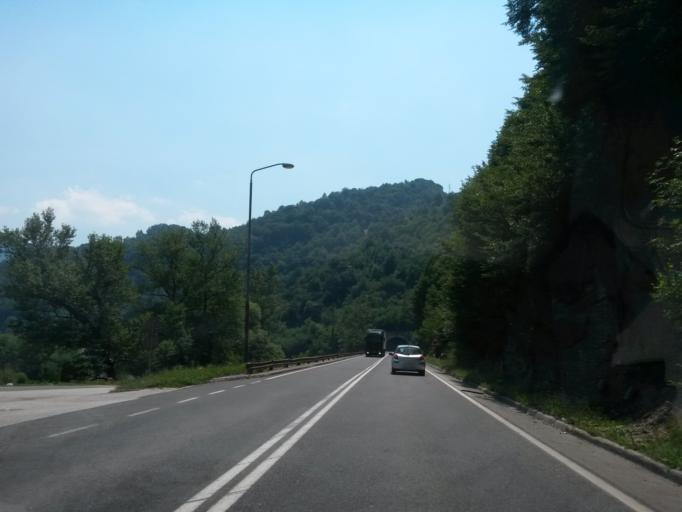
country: BA
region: Federation of Bosnia and Herzegovina
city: Zeljezno Polje
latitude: 44.3031
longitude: 17.9087
